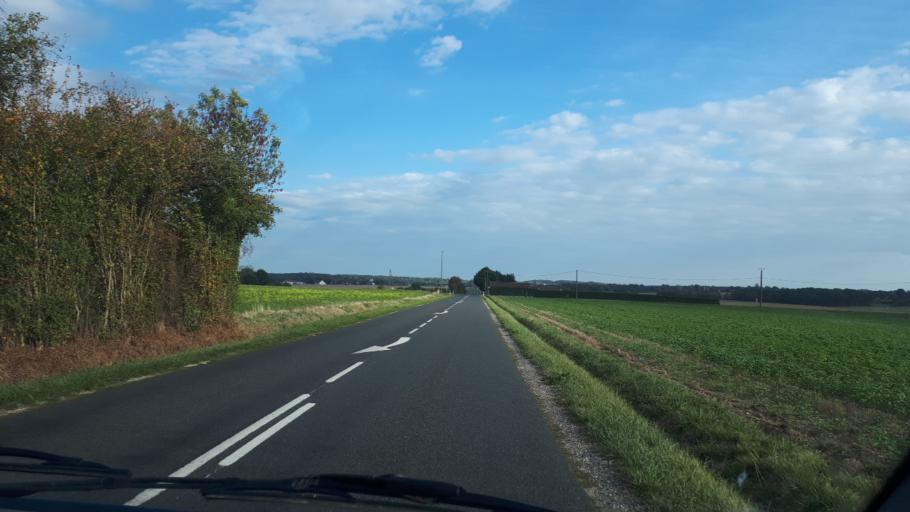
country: FR
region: Centre
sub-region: Departement du Loir-et-Cher
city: Sarge-sur-Braye
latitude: 47.9040
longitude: 0.9301
